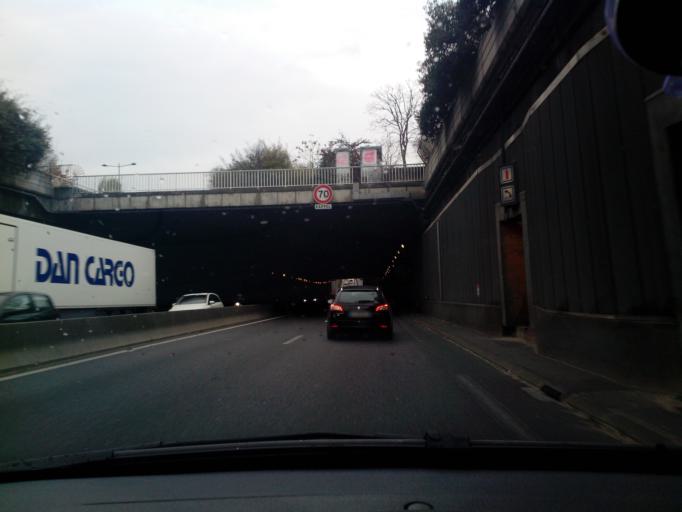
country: FR
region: Ile-de-France
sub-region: Departement du Val-de-Marne
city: Fresnes
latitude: 48.7601
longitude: 2.3210
